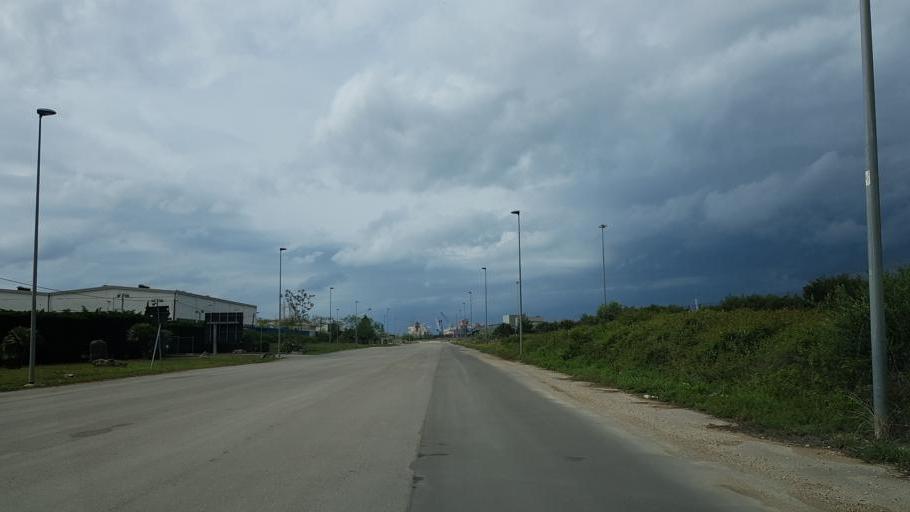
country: IT
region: Apulia
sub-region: Provincia di Brindisi
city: Materdomini
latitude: 40.6386
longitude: 17.9753
